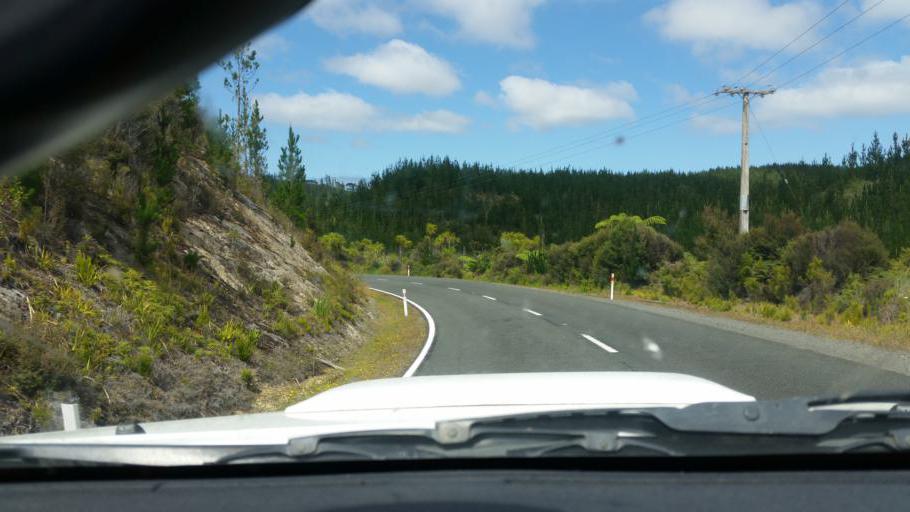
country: NZ
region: Northland
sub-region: Kaipara District
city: Dargaville
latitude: -35.8182
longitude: 173.7114
